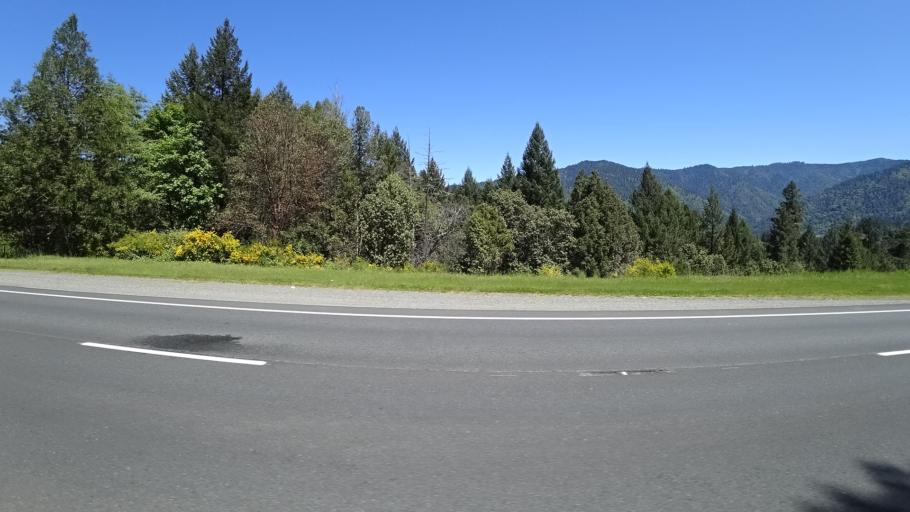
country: US
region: California
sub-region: Humboldt County
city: Willow Creek
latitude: 40.9443
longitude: -123.6483
